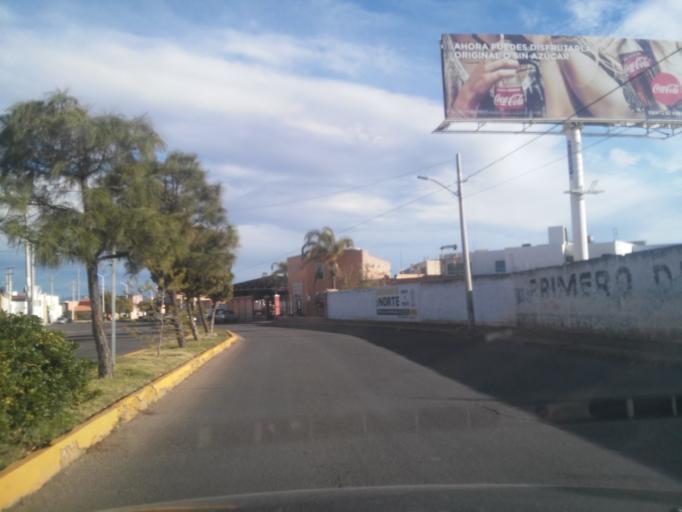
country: MX
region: Durango
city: Victoria de Durango
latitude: 24.0016
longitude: -104.6426
